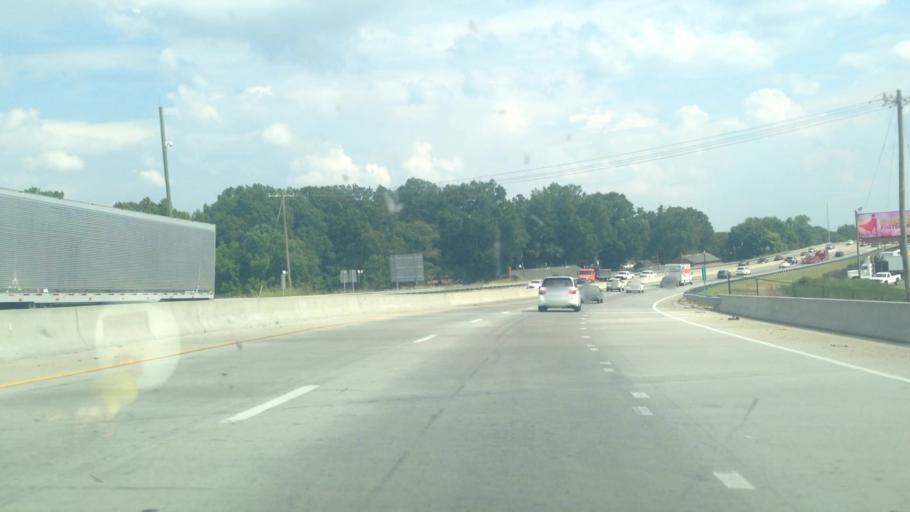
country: US
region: North Carolina
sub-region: Forsyth County
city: Winston-Salem
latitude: 36.1271
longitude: -80.2334
